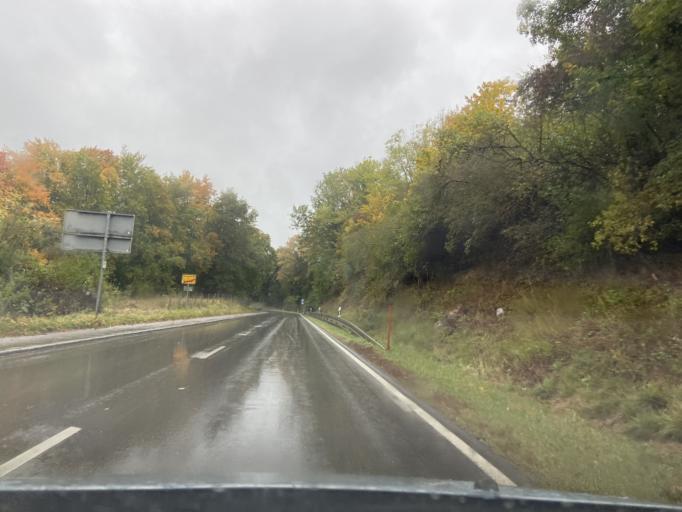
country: DE
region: Baden-Wuerttemberg
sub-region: Tuebingen Region
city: Scheer
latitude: 48.0767
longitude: 9.2951
